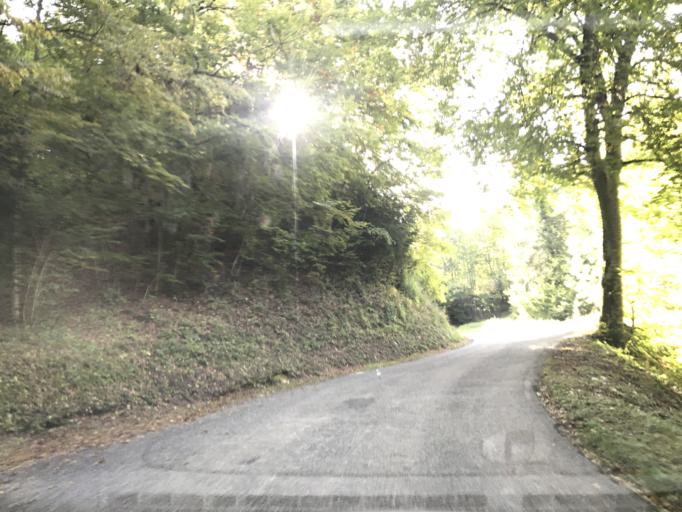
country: FR
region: Rhone-Alpes
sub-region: Departement de la Savoie
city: Novalaise
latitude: 45.6384
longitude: 5.7991
